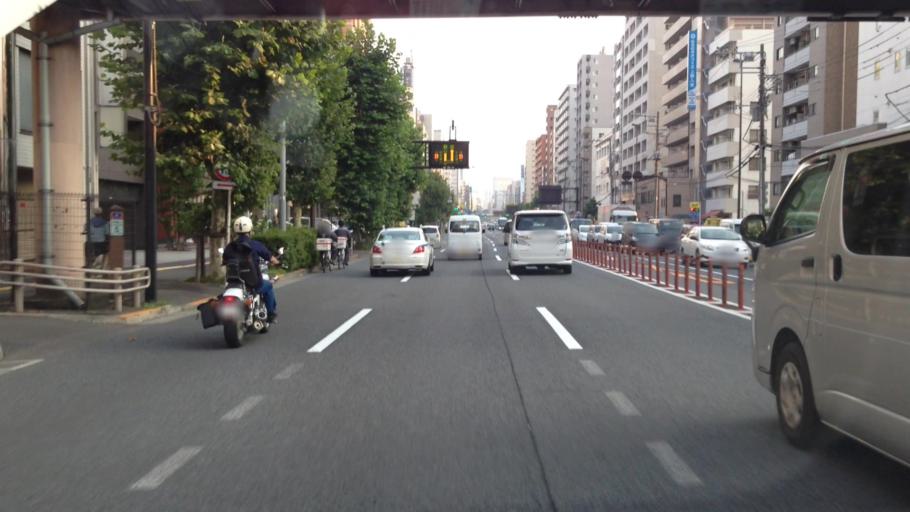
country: JP
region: Saitama
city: Soka
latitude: 35.7245
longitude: 139.7875
